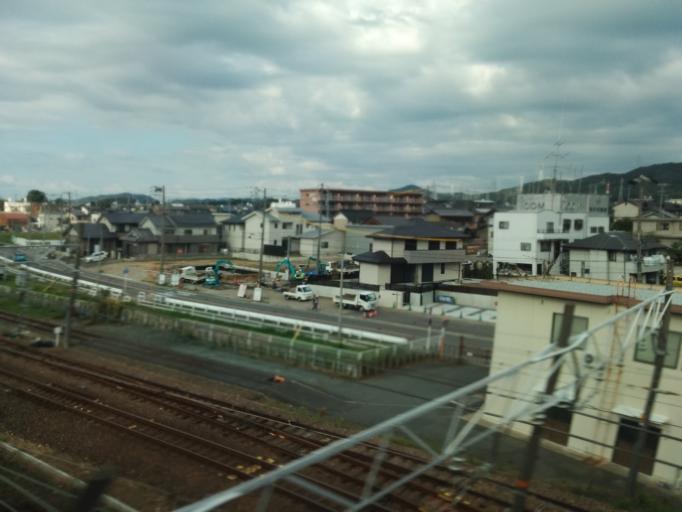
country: JP
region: Aichi
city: Gamagori
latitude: 34.8578
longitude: 137.1647
